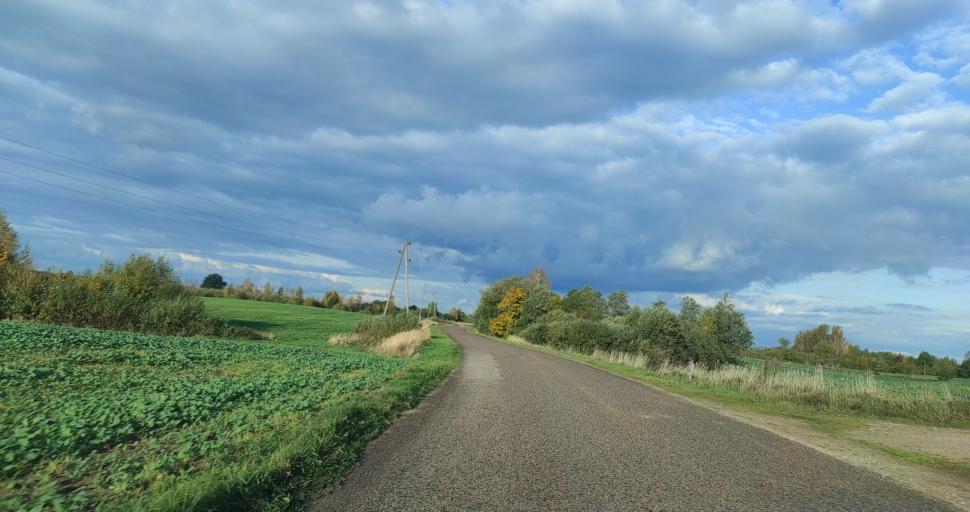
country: LV
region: Aizpute
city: Aizpute
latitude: 56.7800
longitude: 21.7737
